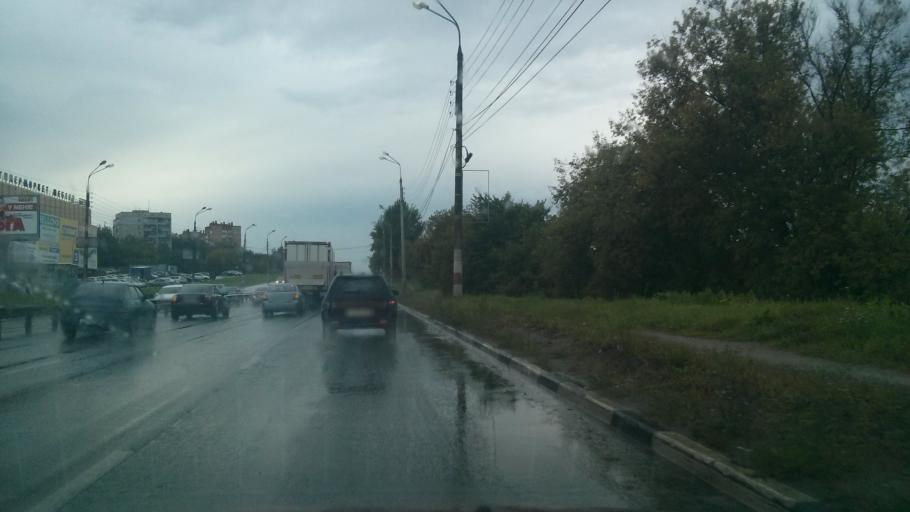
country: RU
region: Nizjnij Novgorod
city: Nizhniy Novgorod
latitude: 56.2419
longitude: 43.9787
